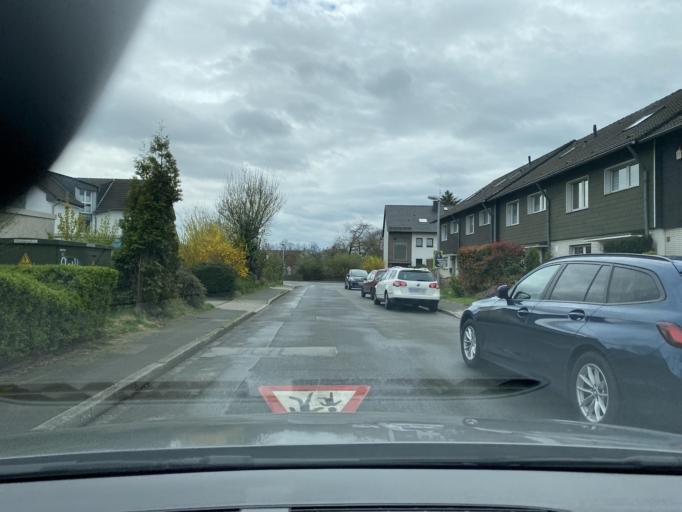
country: DE
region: North Rhine-Westphalia
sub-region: Regierungsbezirk Dusseldorf
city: Muelheim (Ruhr)
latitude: 51.4432
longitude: 6.9160
